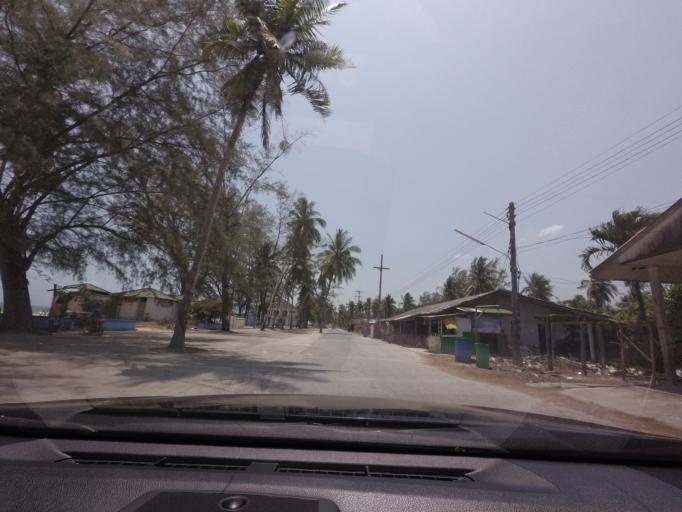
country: TH
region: Pattani
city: Yaring
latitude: 6.8985
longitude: 101.3722
